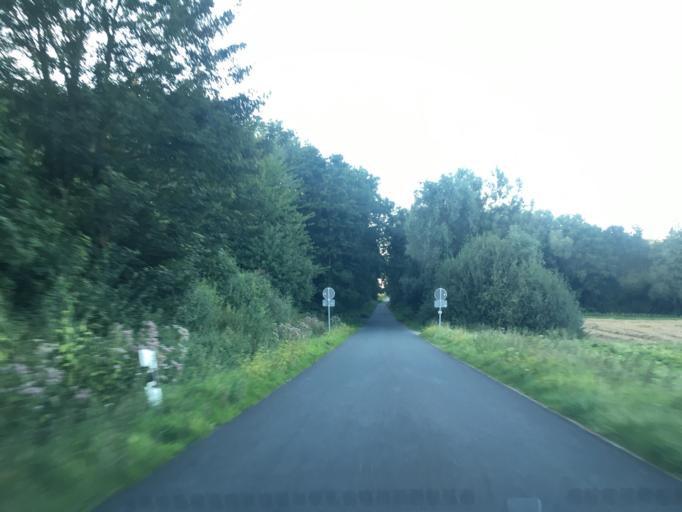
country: DE
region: North Rhine-Westphalia
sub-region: Regierungsbezirk Munster
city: Muenster
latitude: 51.9422
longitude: 7.5524
